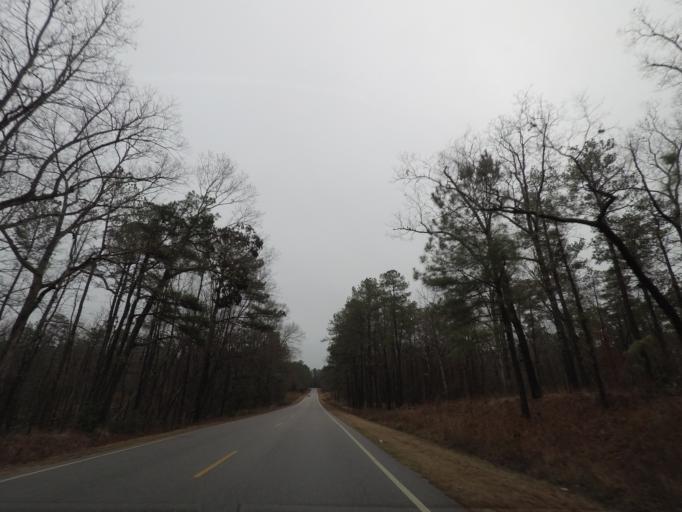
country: US
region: North Carolina
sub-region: Cumberland County
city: Spring Lake
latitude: 35.2622
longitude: -78.9934
